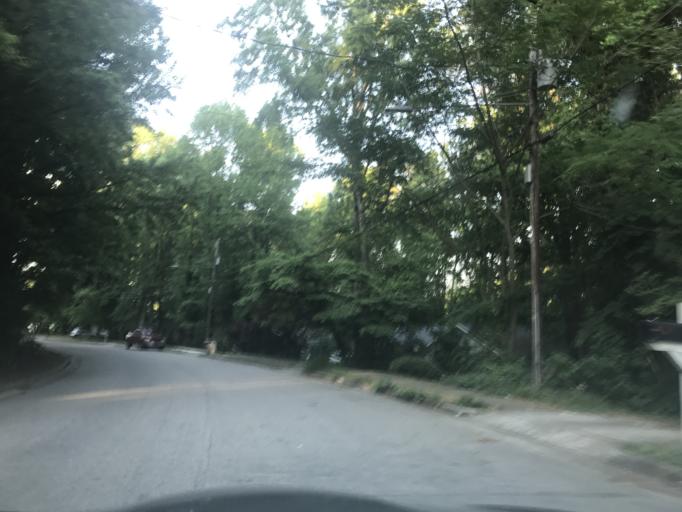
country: US
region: North Carolina
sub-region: Wake County
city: Raleigh
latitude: 35.7493
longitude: -78.6623
